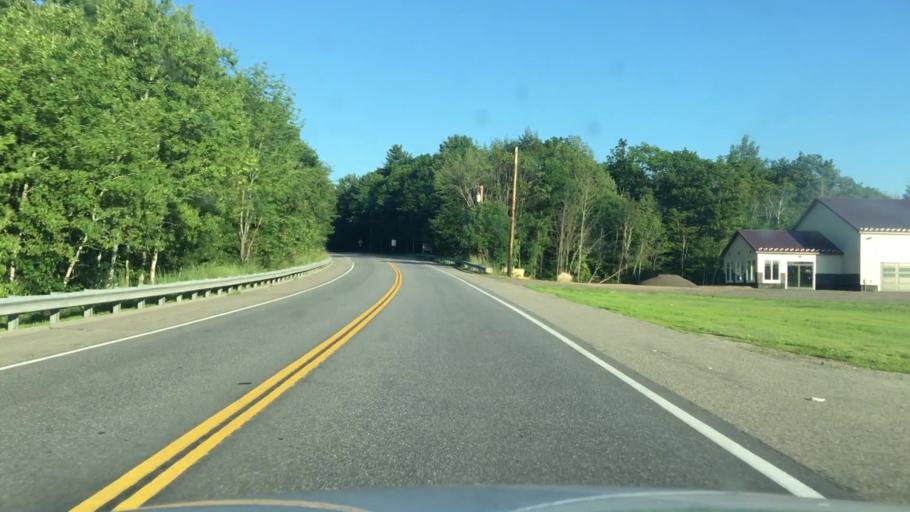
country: US
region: Maine
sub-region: Androscoggin County
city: Lisbon Falls
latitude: 44.0077
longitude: -70.0816
